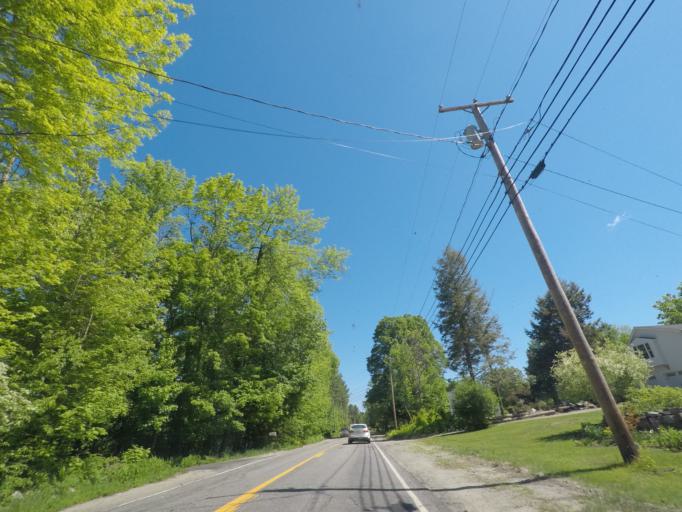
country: US
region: Maine
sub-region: Kennebec County
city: Manchester
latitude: 44.3094
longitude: -69.8776
